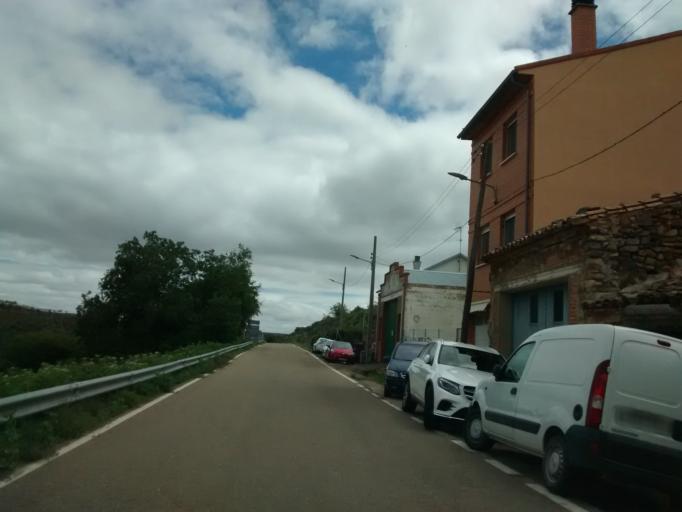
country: ES
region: Aragon
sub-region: Provincia de Zaragoza
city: Lituenigo
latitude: 41.8351
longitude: -1.7590
